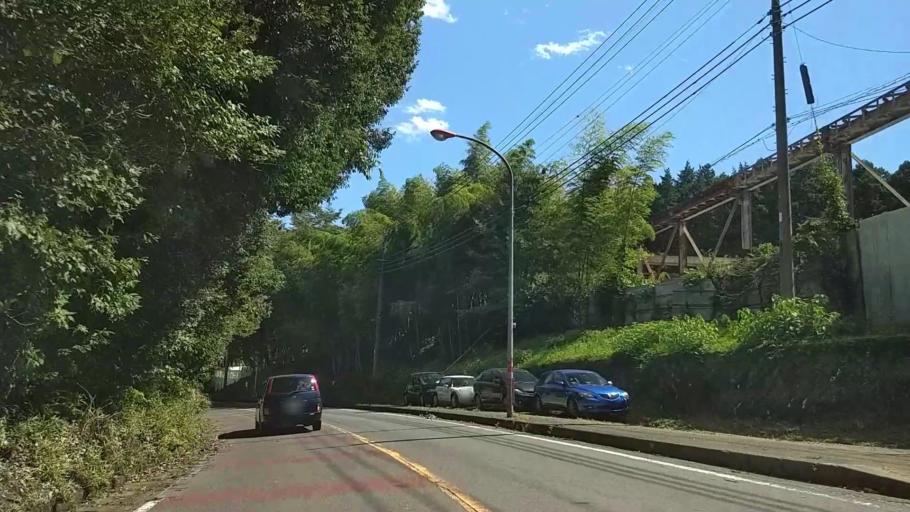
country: JP
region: Tokyo
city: Hachioji
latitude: 35.5502
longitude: 139.2903
